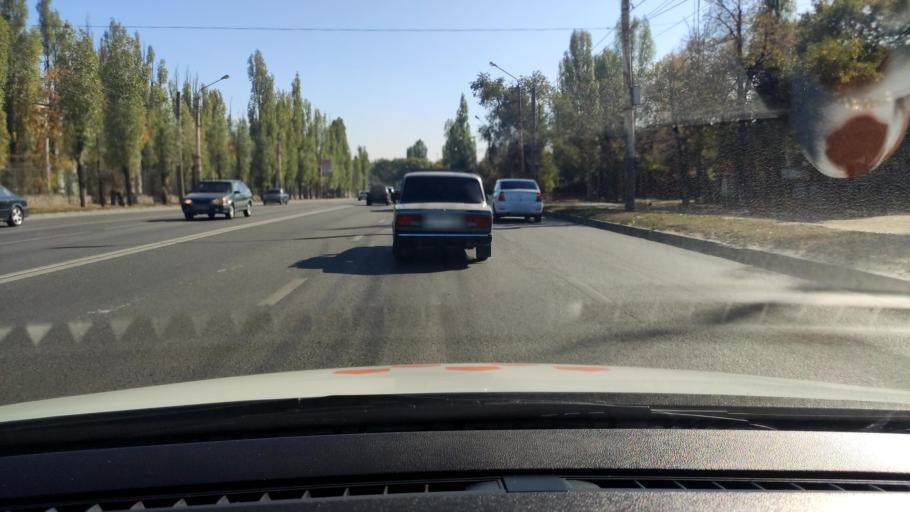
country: RU
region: Voronezj
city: Voronezh
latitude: 51.6262
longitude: 39.2315
